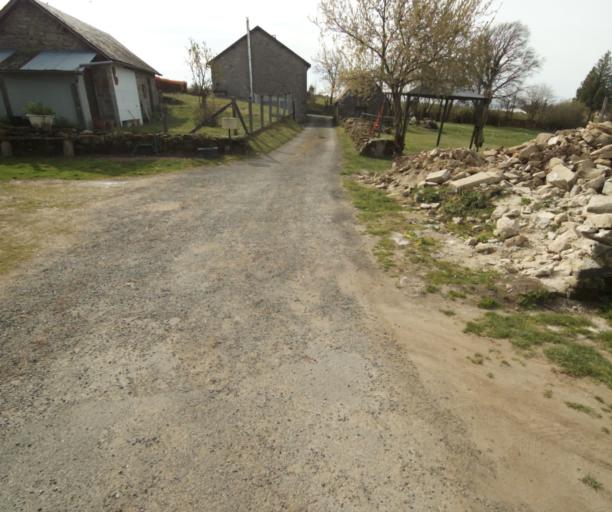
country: FR
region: Limousin
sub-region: Departement de la Correze
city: Correze
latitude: 45.4033
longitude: 1.8265
